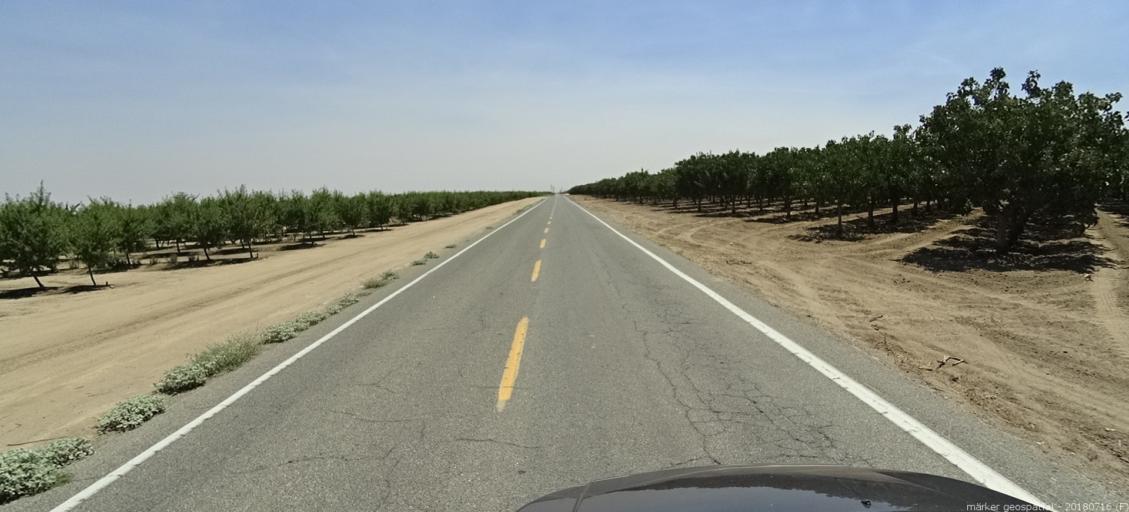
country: US
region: California
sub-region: Madera County
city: Fairmead
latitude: 37.0474
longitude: -120.1448
